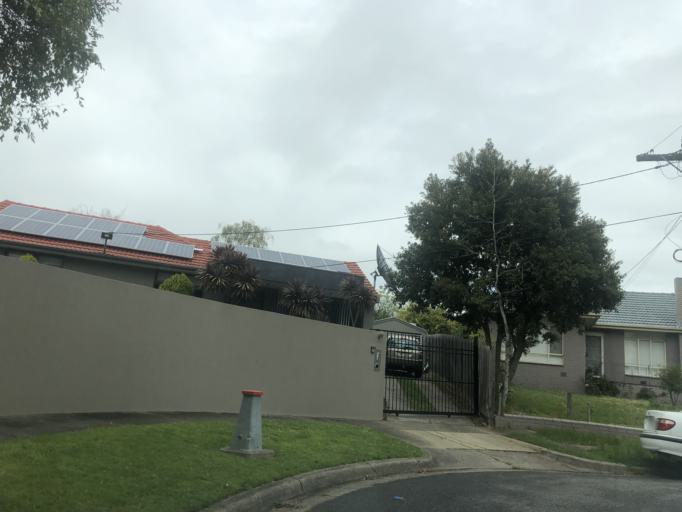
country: AU
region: Victoria
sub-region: Greater Dandenong
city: Dandenong North
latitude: -37.9658
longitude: 145.2168
